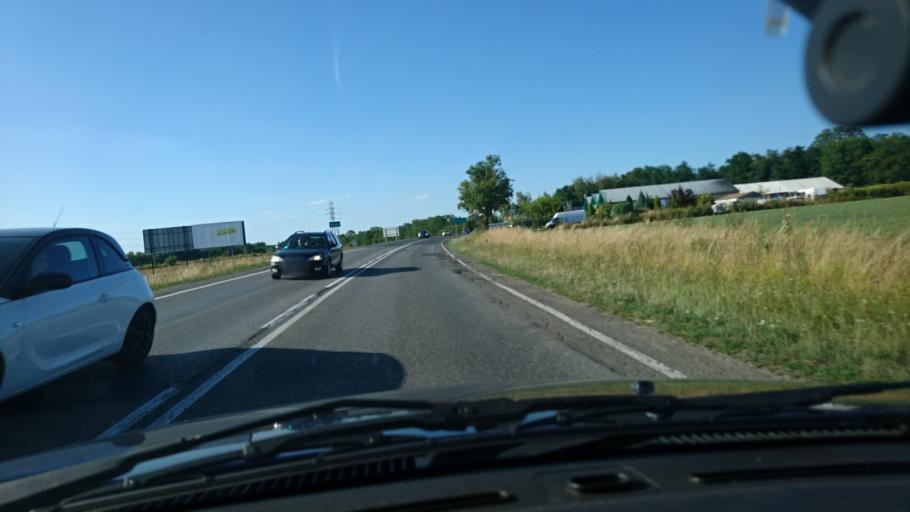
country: PL
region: Silesian Voivodeship
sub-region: Powiat gliwicki
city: Pyskowice
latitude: 50.3711
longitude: 18.6353
